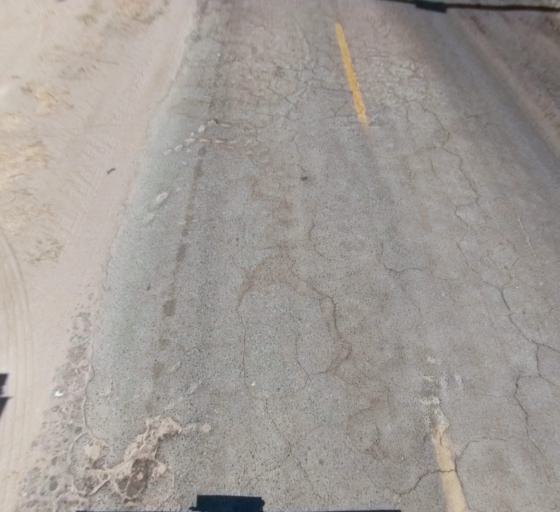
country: US
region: California
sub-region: Fresno County
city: Biola
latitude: 36.8529
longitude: -120.0374
